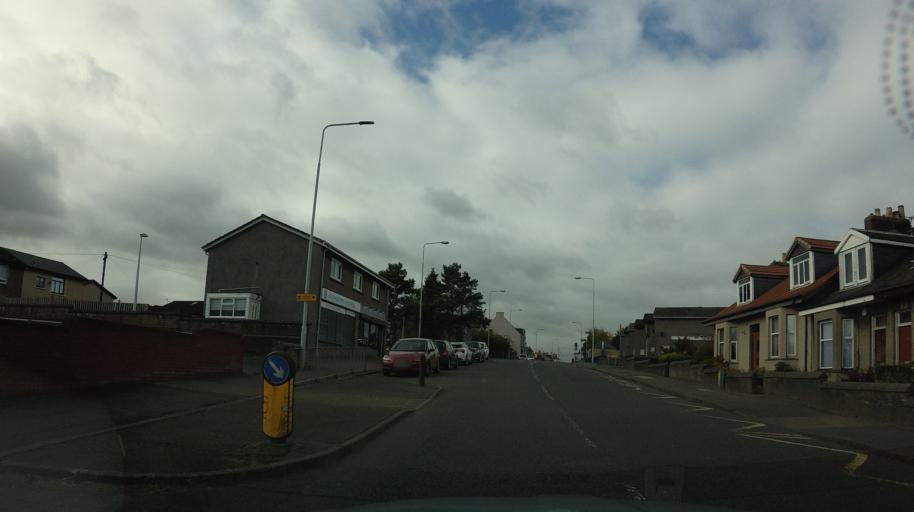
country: GB
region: Scotland
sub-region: Fife
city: Cowdenbeath
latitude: 56.1067
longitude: -3.3447
